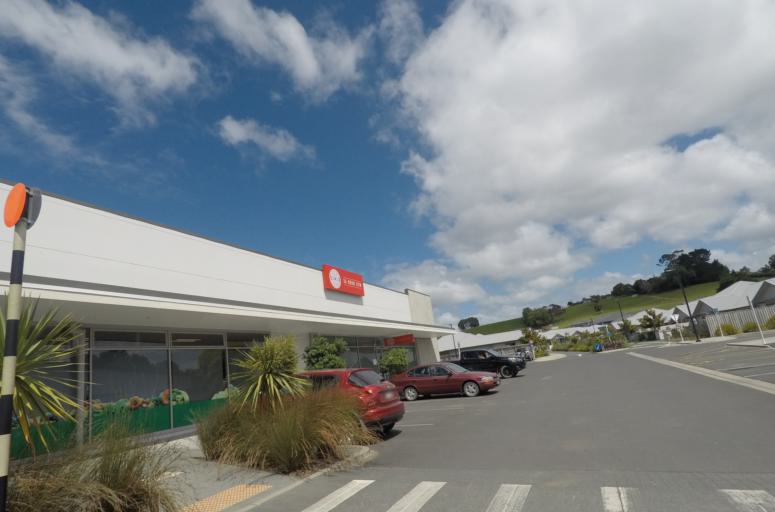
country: NZ
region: Auckland
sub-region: Auckland
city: Warkworth
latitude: -36.4095
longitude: 174.6603
